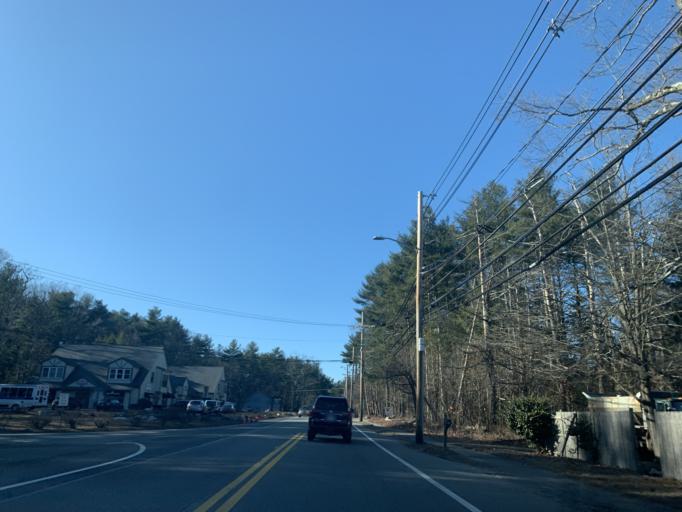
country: US
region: Massachusetts
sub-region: Middlesex County
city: Sudbury
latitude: 42.3603
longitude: -71.4368
